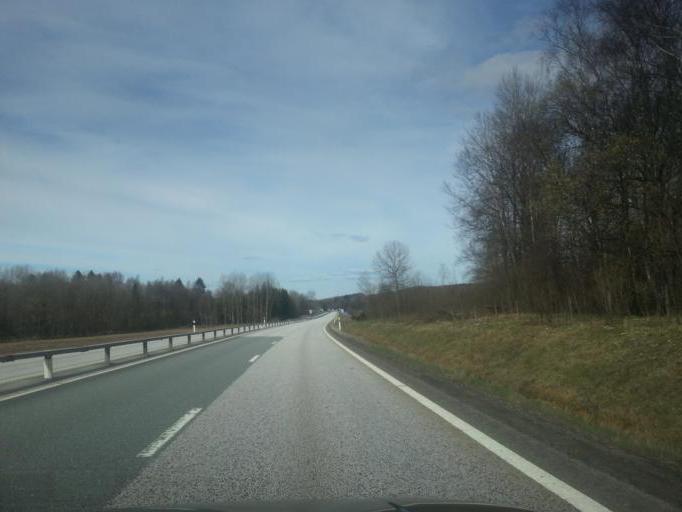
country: SE
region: Joenkoeping
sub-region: Jonkopings Kommun
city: Bankeryd
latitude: 57.8082
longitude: 14.0973
